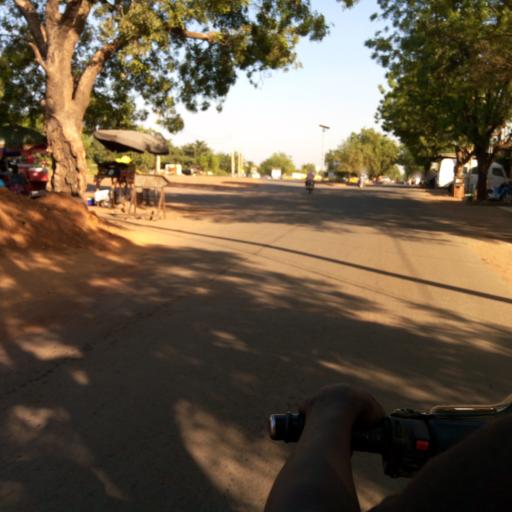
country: ML
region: Bamako
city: Bamako
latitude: 12.6566
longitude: -8.0274
